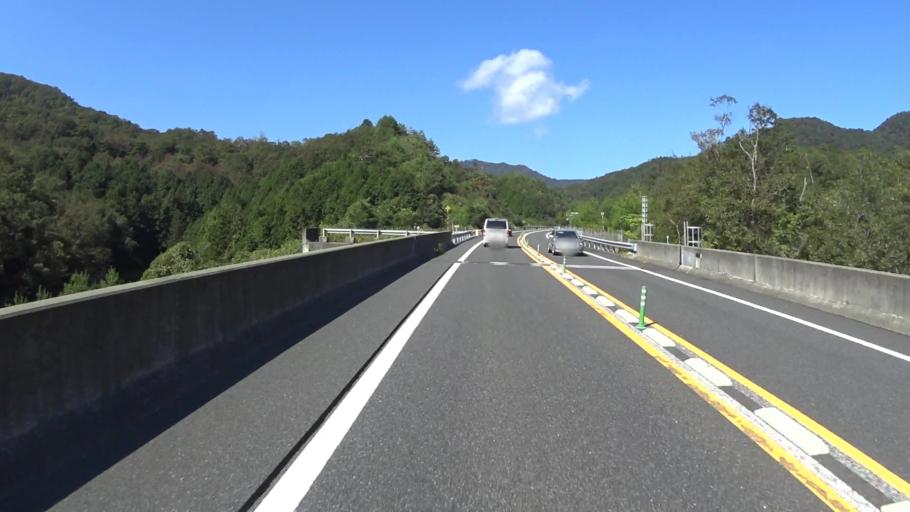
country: JP
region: Kyoto
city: Miyazu
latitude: 35.4499
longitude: 135.1823
